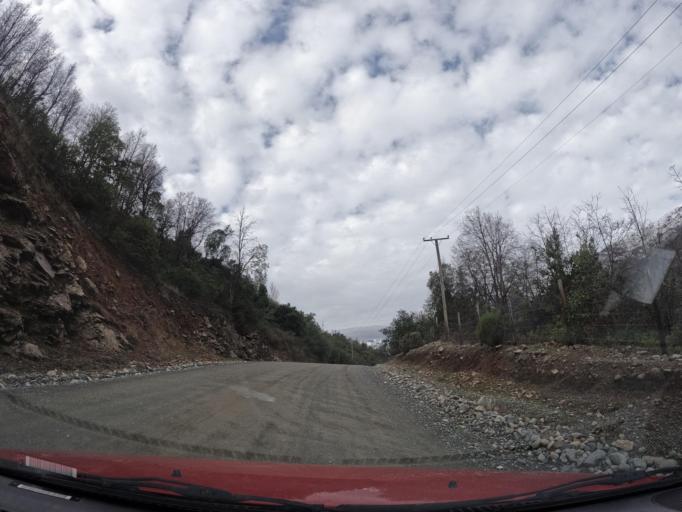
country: CL
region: Maule
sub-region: Provincia de Linares
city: Colbun
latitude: -35.8584
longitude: -71.2393
